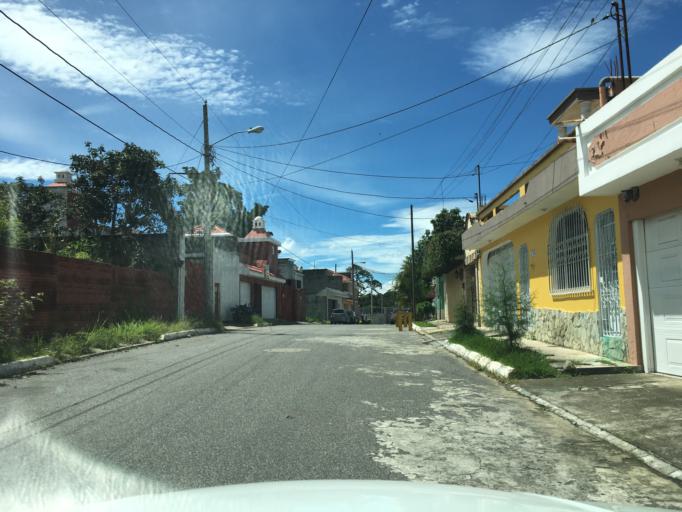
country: GT
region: Guatemala
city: Mixco
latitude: 14.6559
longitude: -90.5647
